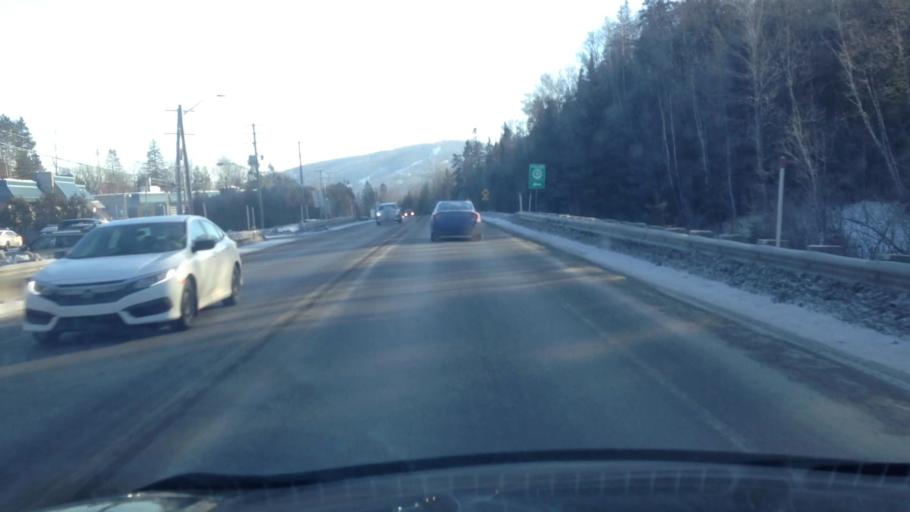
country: CA
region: Quebec
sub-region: Laurentides
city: Saint-Sauveur
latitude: 45.8859
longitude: -74.1834
